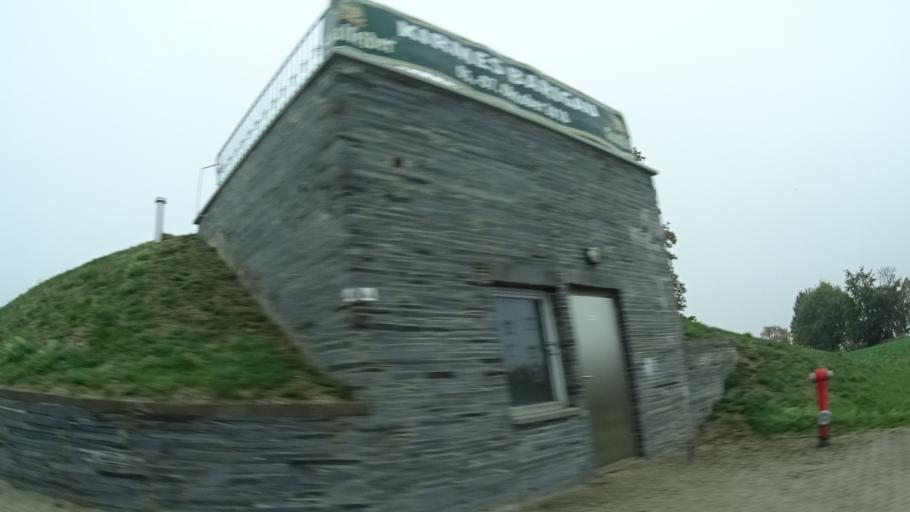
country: DE
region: Thuringia
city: Mellenbach-Glasbach
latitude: 50.6293
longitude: 11.1072
